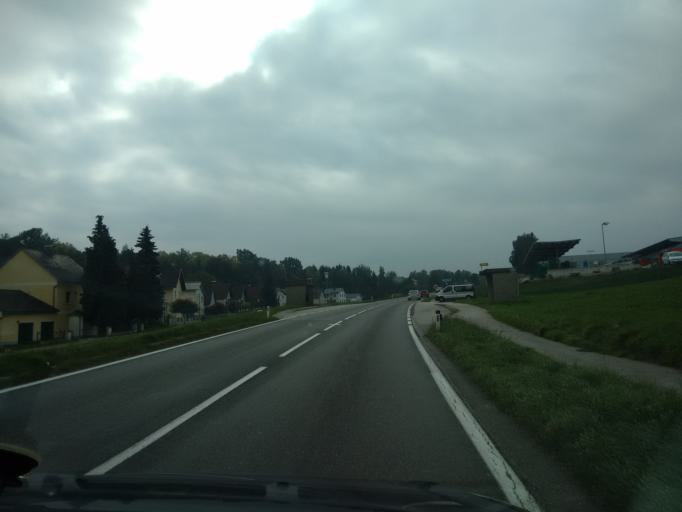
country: AT
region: Upper Austria
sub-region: Politischer Bezirk Steyr-Land
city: Bad Hall
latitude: 48.0453
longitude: 14.2078
